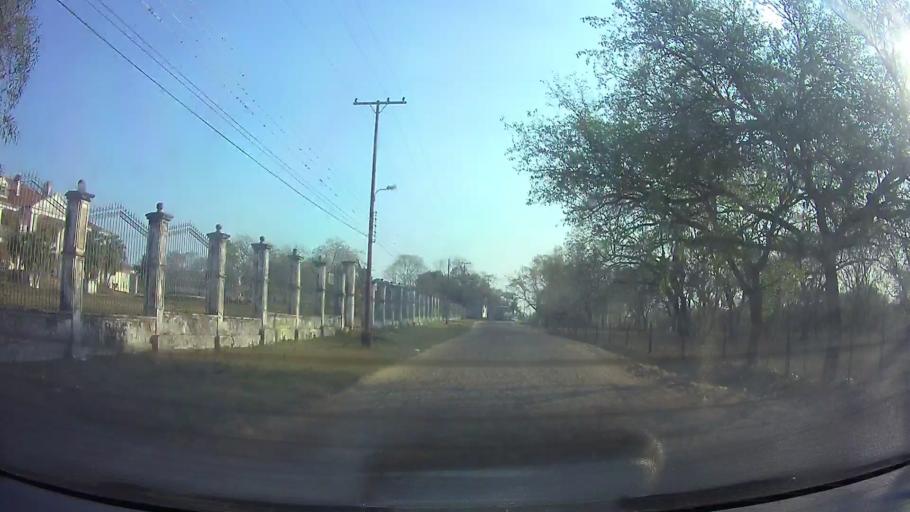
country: PY
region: Central
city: Limpio
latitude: -25.2208
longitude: -57.5041
